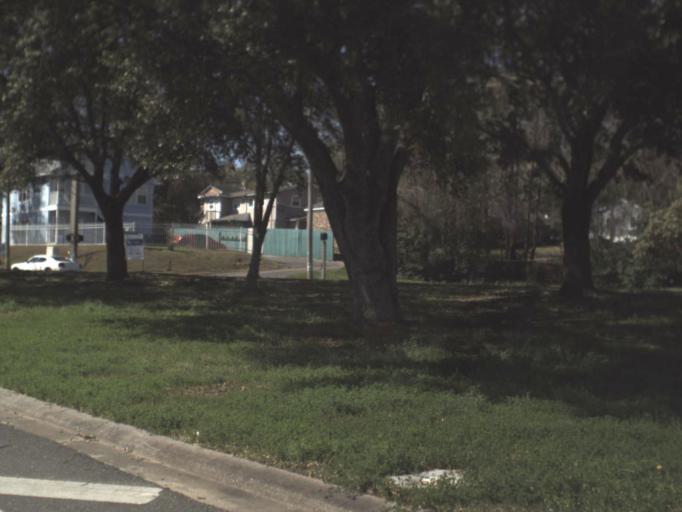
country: US
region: Florida
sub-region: Leon County
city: Tallahassee
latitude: 30.4290
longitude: -84.2819
